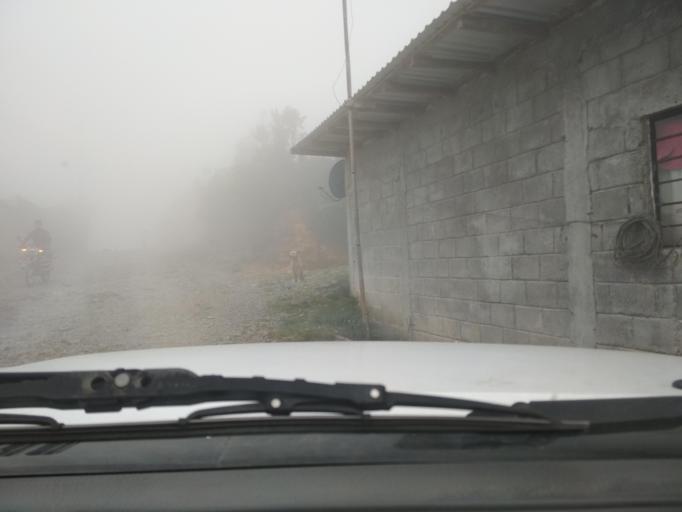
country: MX
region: Veracruz
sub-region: La Perla
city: Barrio de San Miguel
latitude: 18.9416
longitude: -97.1183
